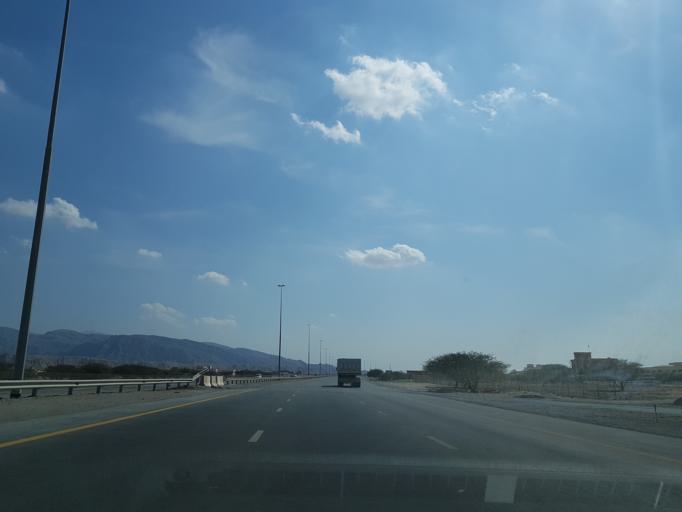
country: AE
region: Ra's al Khaymah
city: Ras al-Khaimah
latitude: 25.8077
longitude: 56.0299
